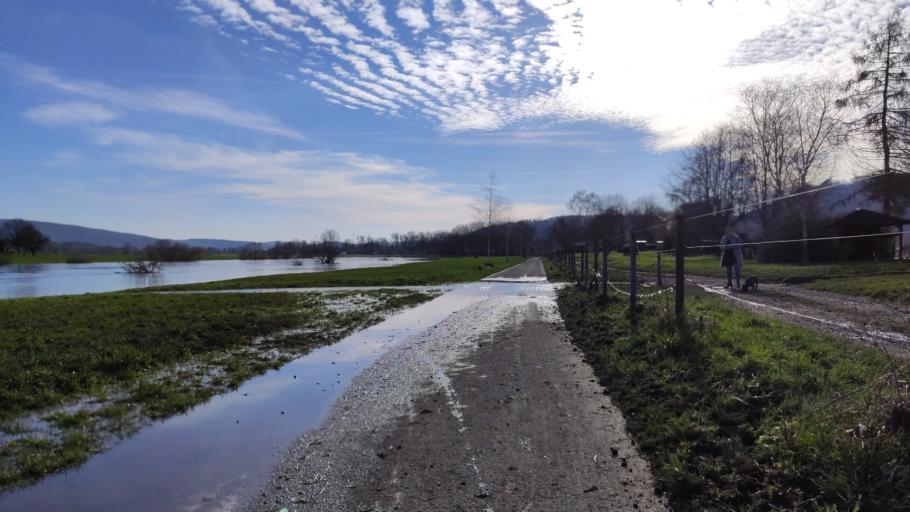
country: DE
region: Lower Saxony
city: Boffzen
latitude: 51.7485
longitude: 9.3803
